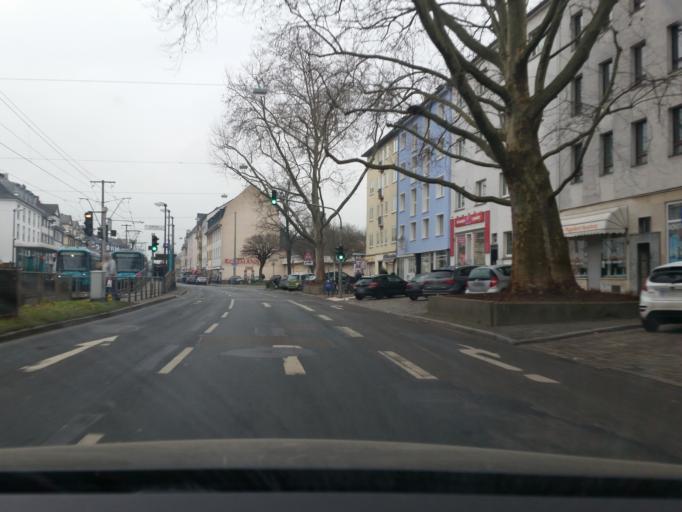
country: DE
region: Hesse
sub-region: Regierungsbezirk Darmstadt
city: Frankfurt am Main
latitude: 50.1362
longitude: 8.6715
